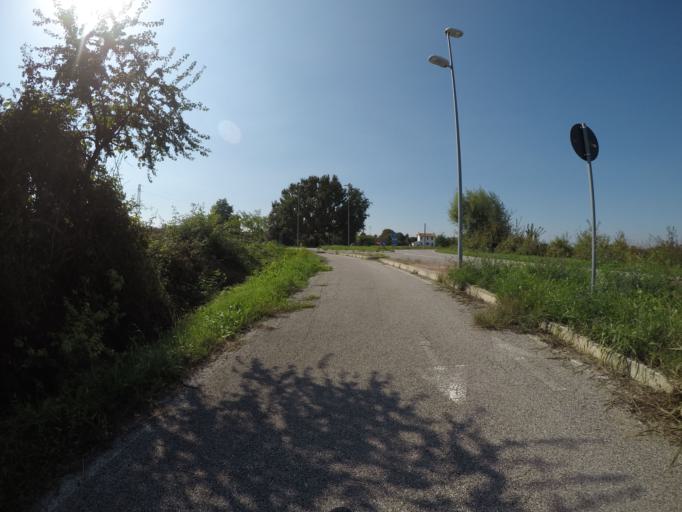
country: IT
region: Veneto
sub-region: Provincia di Rovigo
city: Polesella
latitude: 44.9598
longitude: 11.7284
